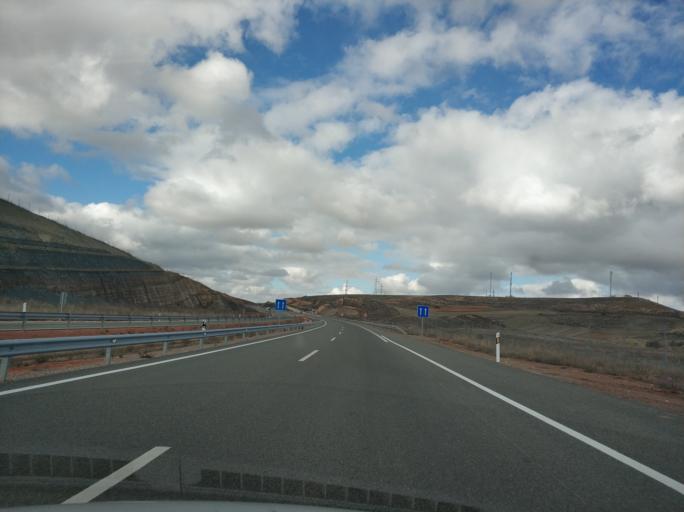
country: ES
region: Castille and Leon
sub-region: Provincia de Soria
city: Yelo
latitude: 41.2243
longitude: -2.4728
